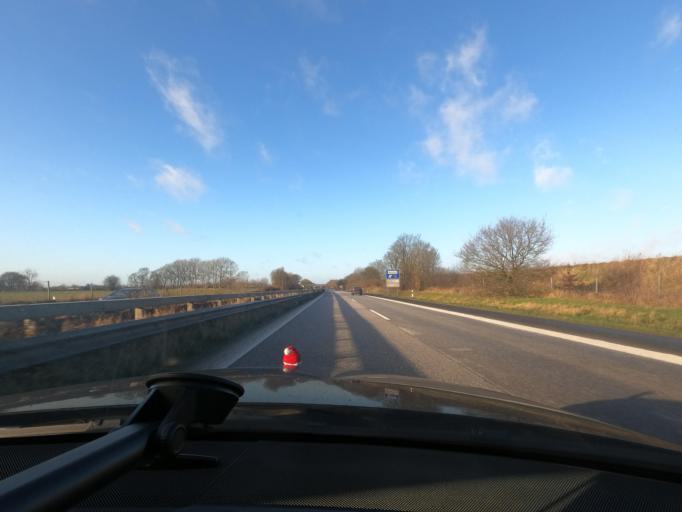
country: DE
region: Schleswig-Holstein
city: Selk
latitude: 54.4682
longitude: 9.5616
